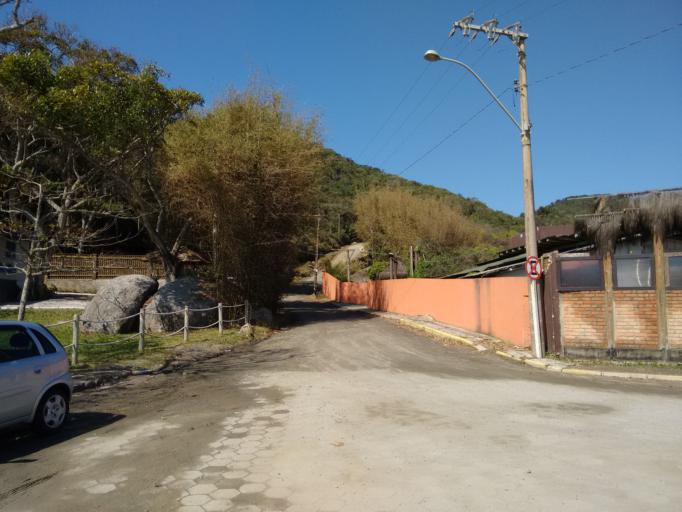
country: BR
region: Santa Catarina
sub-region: Porto Belo
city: Porto Belo
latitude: -27.2029
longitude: -48.4898
